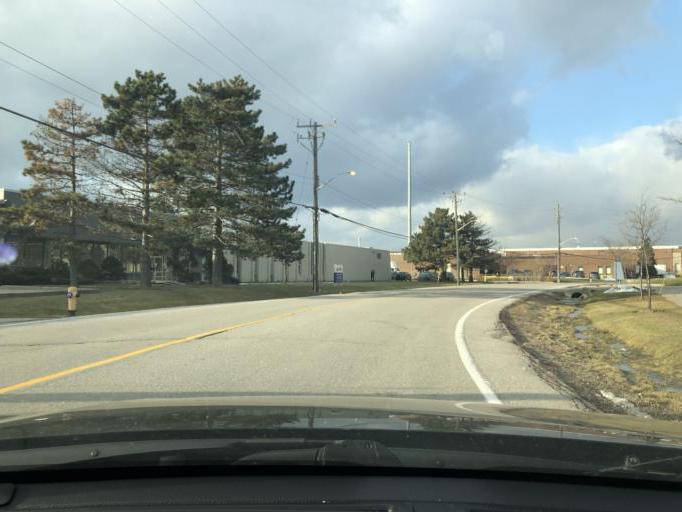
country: CA
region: Ontario
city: Scarborough
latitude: 43.7653
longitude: -79.2946
